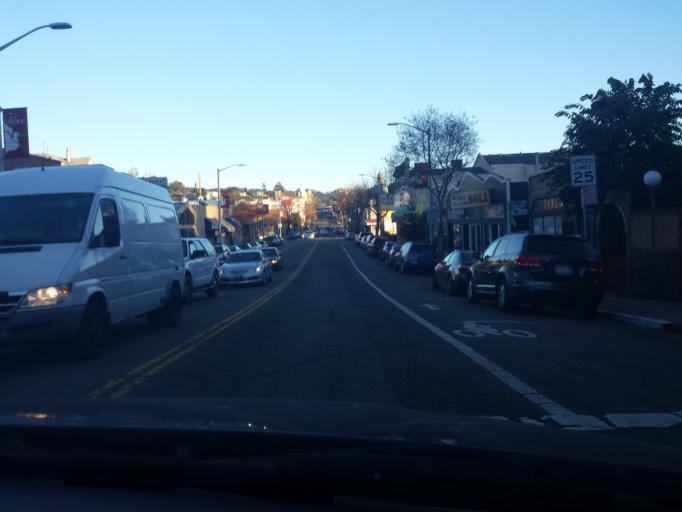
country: US
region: California
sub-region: Alameda County
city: Piedmont
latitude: 37.8009
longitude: -122.2185
